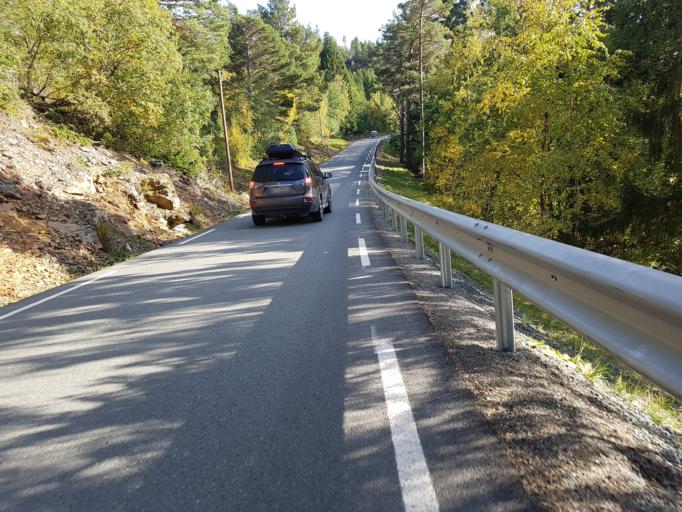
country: NO
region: Sor-Trondelag
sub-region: Malvik
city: Malvik
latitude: 63.3680
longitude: 10.6189
